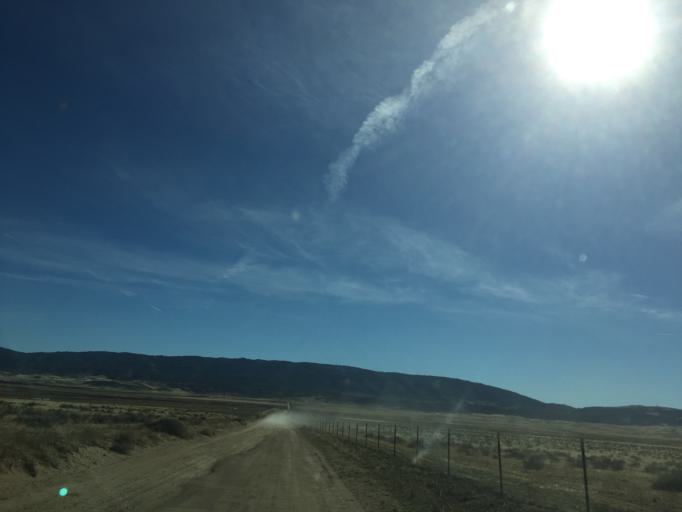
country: US
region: California
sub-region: Kern County
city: Lebec
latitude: 34.8315
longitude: -118.6609
